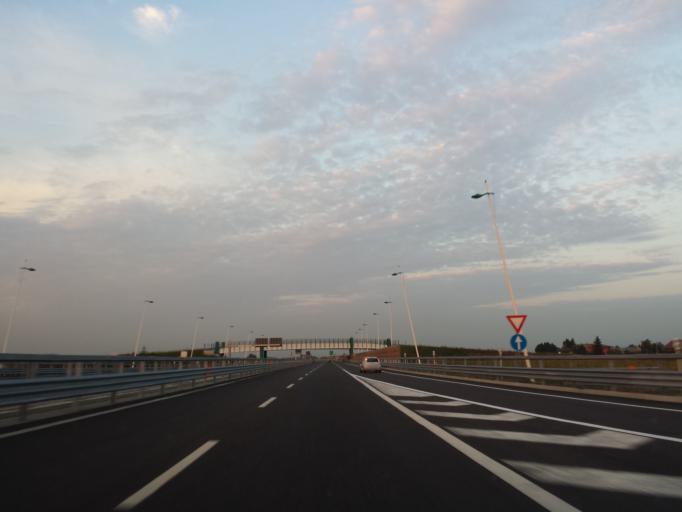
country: IT
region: Veneto
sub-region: Provincia di Padova
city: Bastia
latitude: 45.3923
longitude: 11.6192
